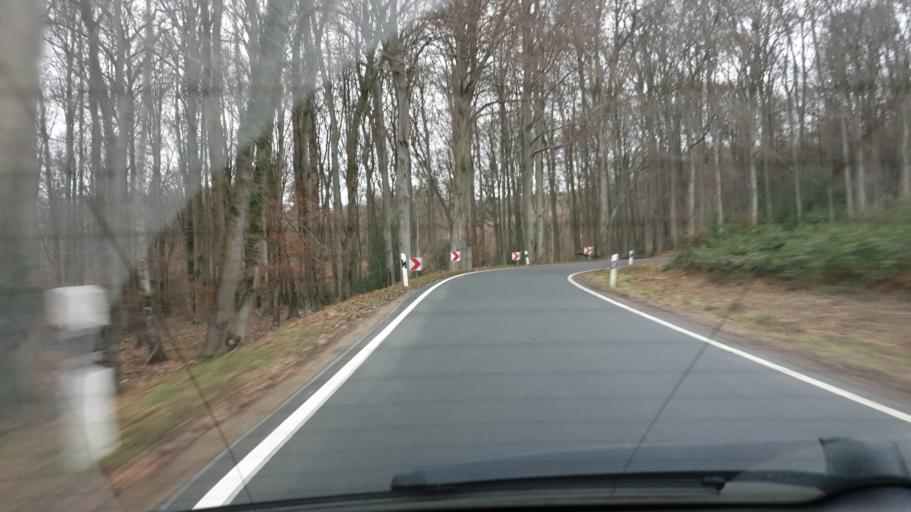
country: DE
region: North Rhine-Westphalia
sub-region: Regierungsbezirk Detmold
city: Lemgo
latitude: 52.0588
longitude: 8.8503
